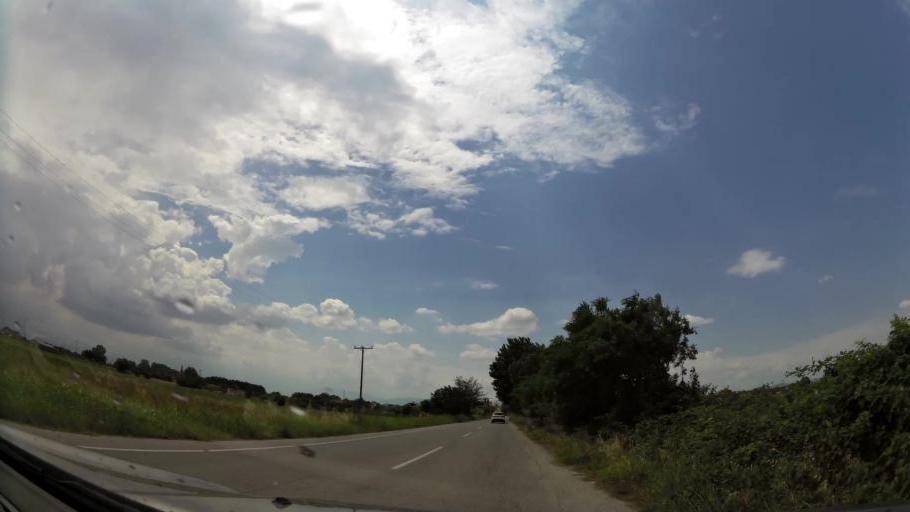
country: GR
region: Central Macedonia
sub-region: Nomos Pierias
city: Korinos
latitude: 40.3122
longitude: 22.5998
